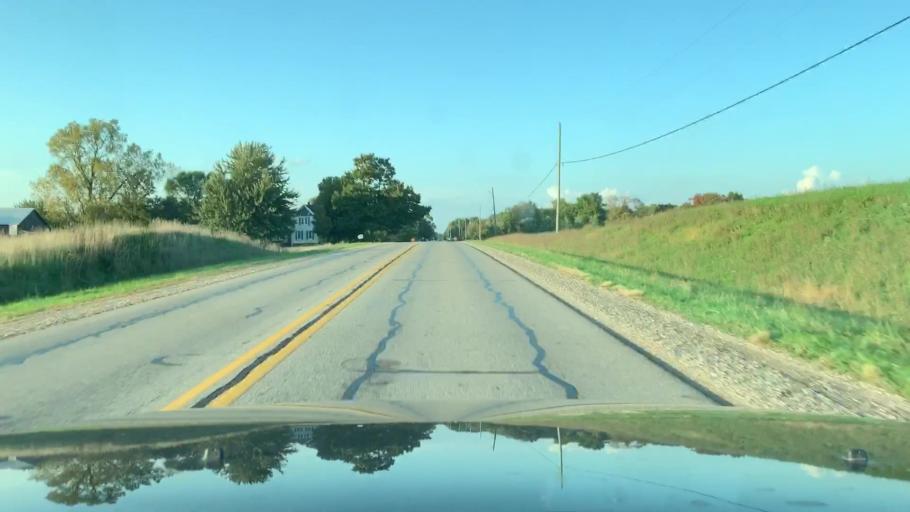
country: US
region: Michigan
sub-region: Ottawa County
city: Hudsonville
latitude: 42.8068
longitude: -85.8420
